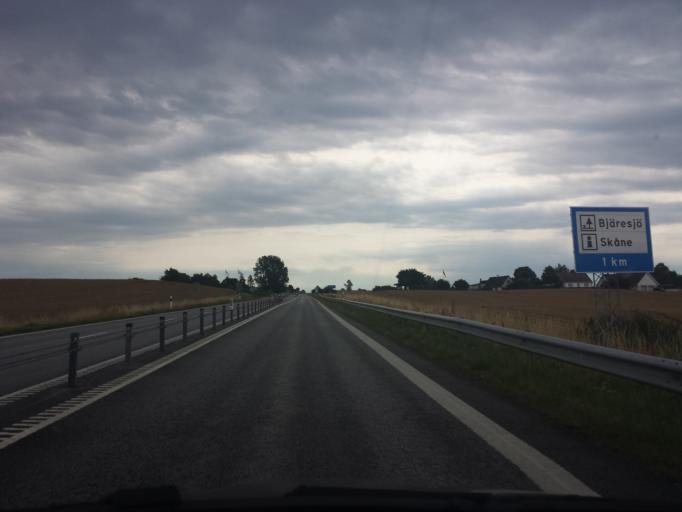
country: SE
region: Skane
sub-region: Ystads Kommun
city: Ystad
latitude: 55.4571
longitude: 13.7407
